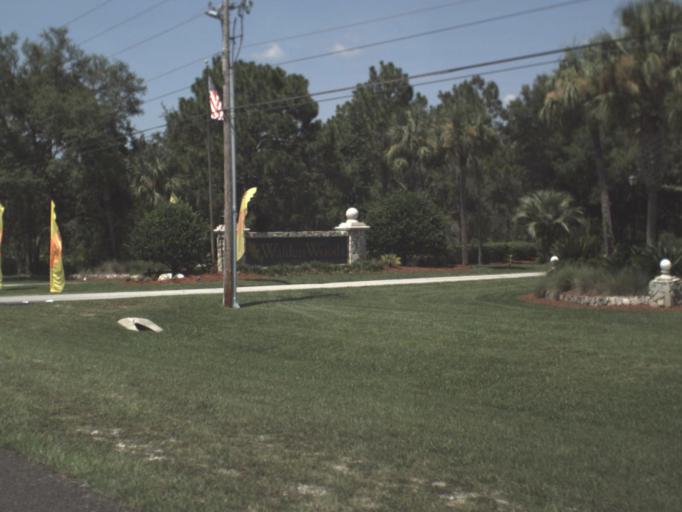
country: US
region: Florida
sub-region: Citrus County
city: Sugarmill Woods
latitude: 28.7095
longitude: -82.5525
